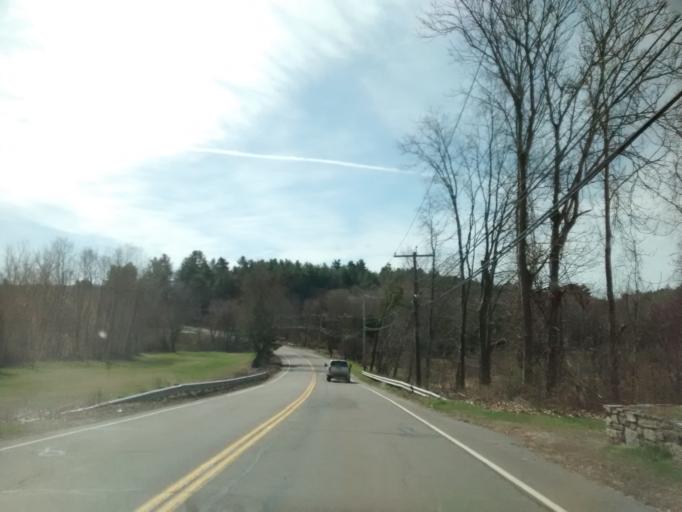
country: US
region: Massachusetts
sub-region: Worcester County
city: Millbury
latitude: 42.1769
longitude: -71.7297
